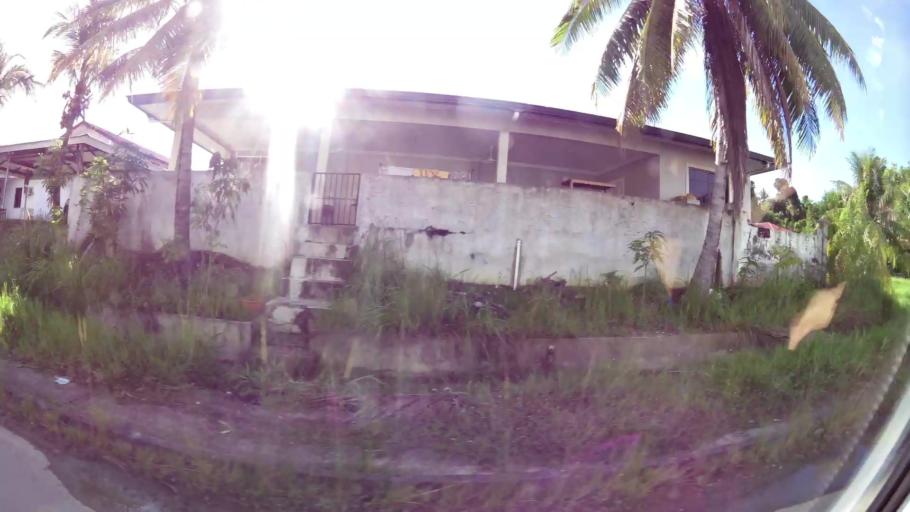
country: BN
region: Brunei and Muara
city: Bandar Seri Begawan
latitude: 4.9735
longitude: 114.9728
